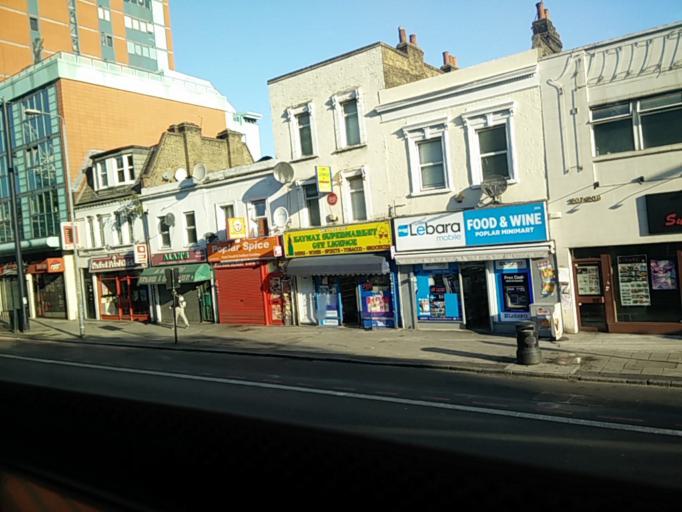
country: GB
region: England
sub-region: Greater London
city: Poplar
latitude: 51.5112
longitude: -0.0119
